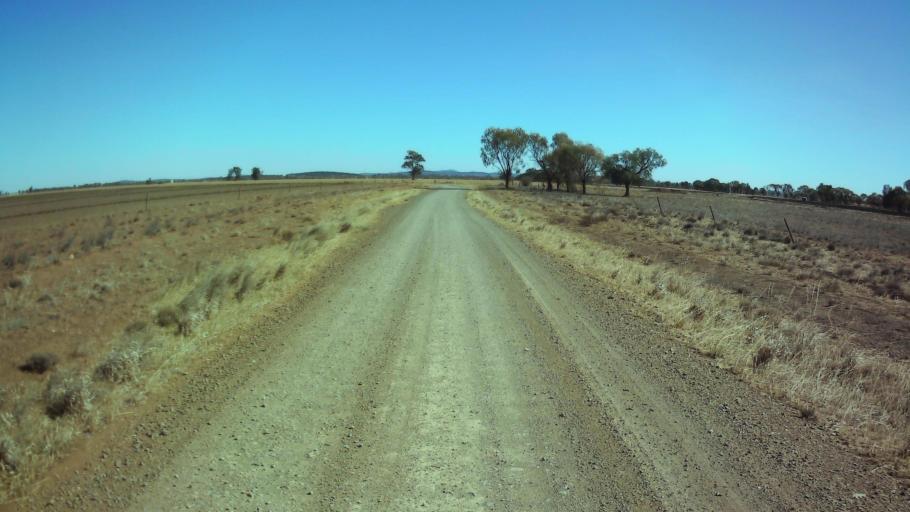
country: AU
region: New South Wales
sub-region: Weddin
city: Grenfell
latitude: -33.8333
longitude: 147.7425
